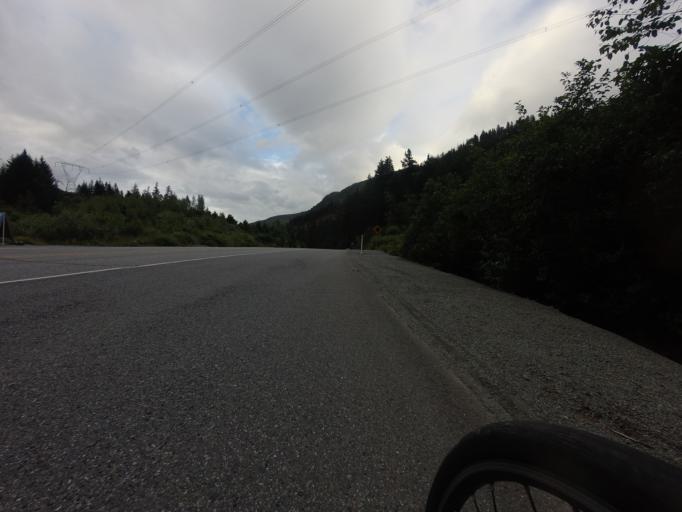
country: CA
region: British Columbia
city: Pemberton
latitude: 50.2872
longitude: -122.8452
